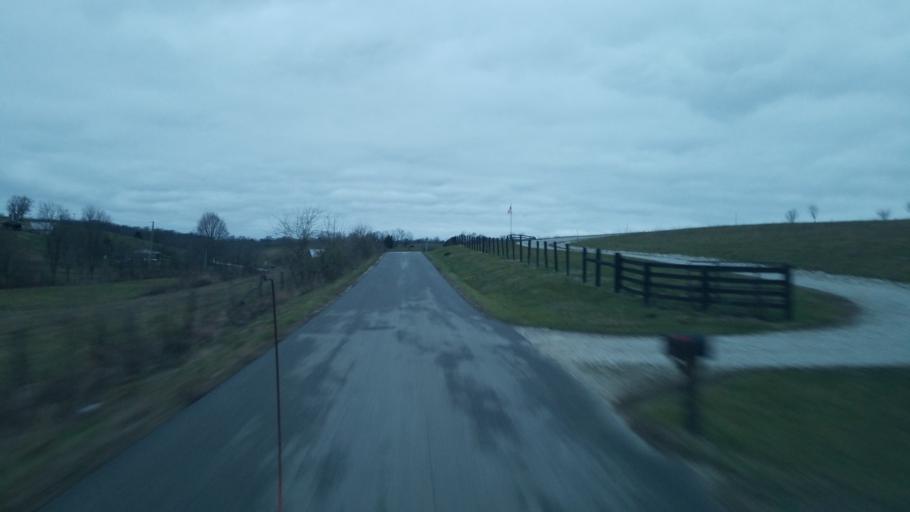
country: US
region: Kentucky
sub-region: Fleming County
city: Flemingsburg
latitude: 38.5037
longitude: -83.6970
